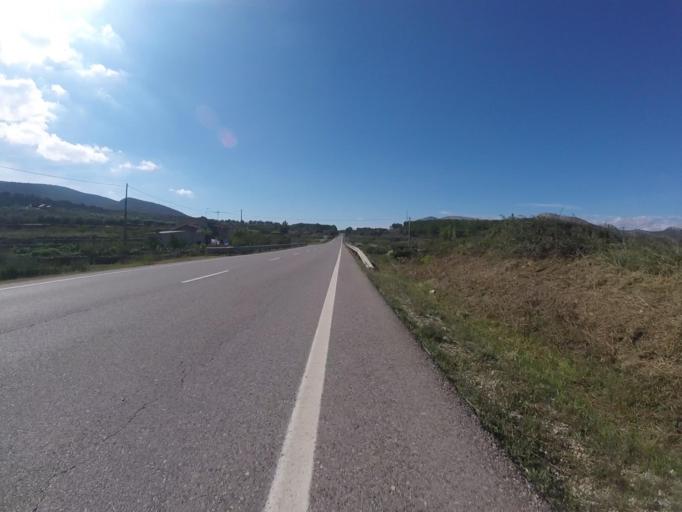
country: ES
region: Valencia
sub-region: Provincia de Castello
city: Sarratella
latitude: 40.3256
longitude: -0.0200
